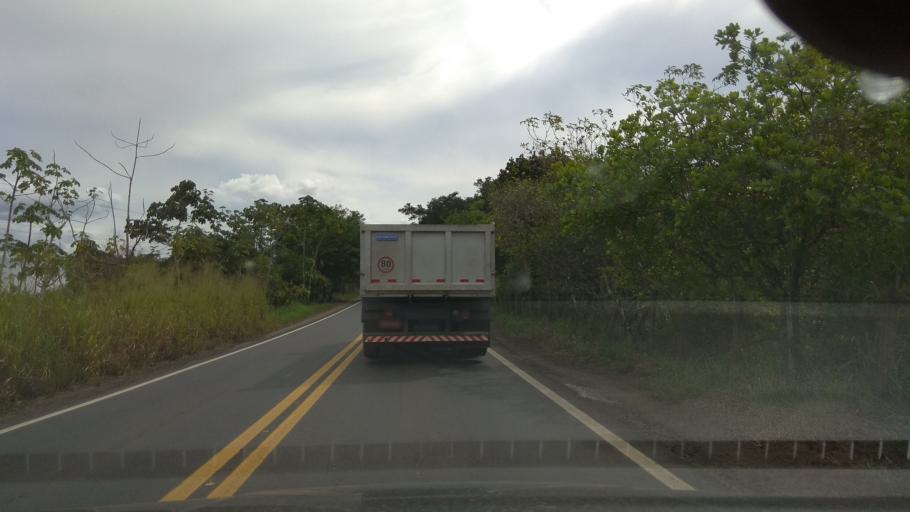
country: BR
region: Bahia
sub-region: Ubata
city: Ubata
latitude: -14.1974
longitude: -39.6148
